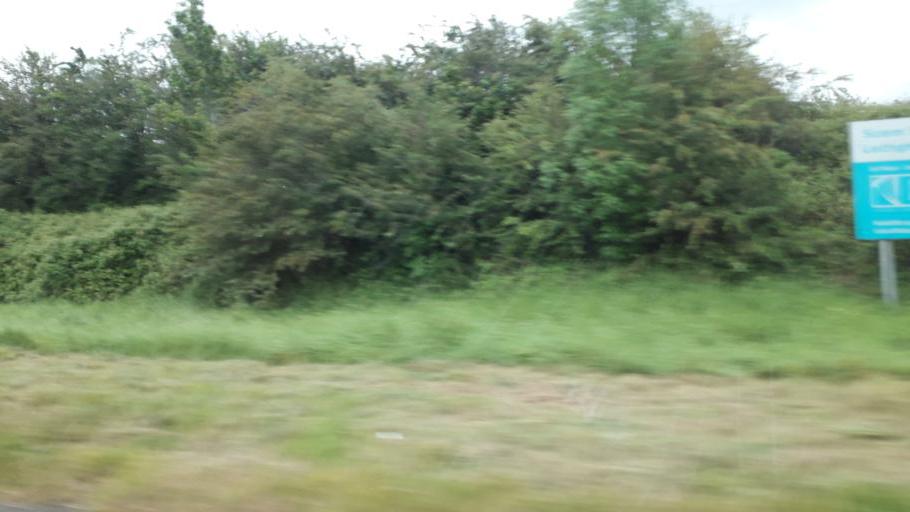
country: IE
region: Leinster
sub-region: County Carlow
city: Bagenalstown
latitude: 52.7363
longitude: -6.9869
